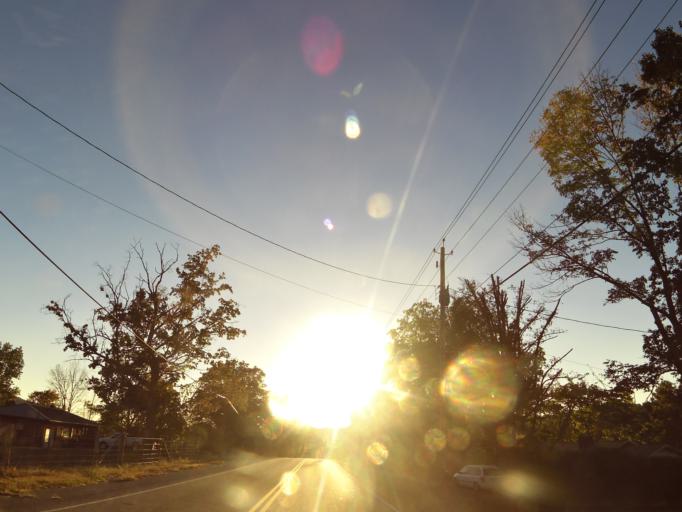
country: US
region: Tennessee
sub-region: Grainger County
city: Rutledge
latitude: 36.2851
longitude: -83.6080
